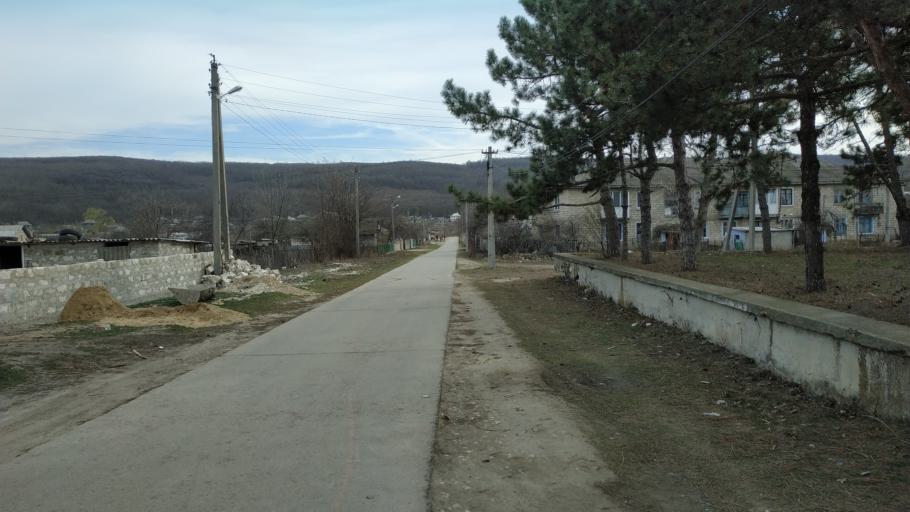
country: MD
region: Hincesti
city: Dancu
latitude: 46.8590
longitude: 28.2502
